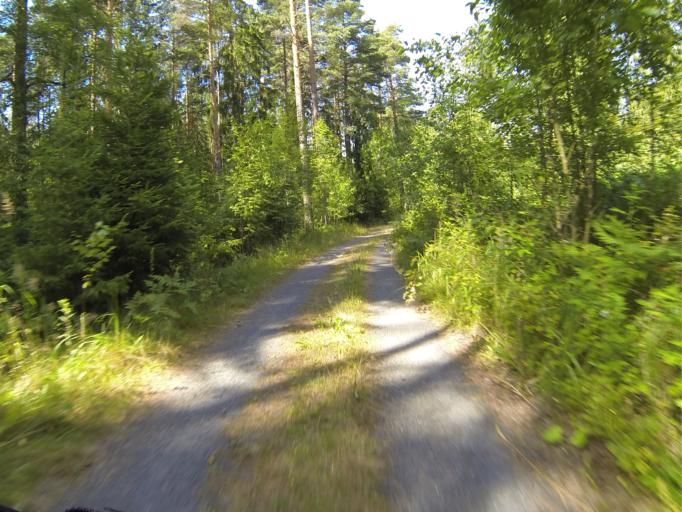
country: FI
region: Varsinais-Suomi
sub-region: Salo
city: Halikko
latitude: 60.2776
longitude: 23.0116
